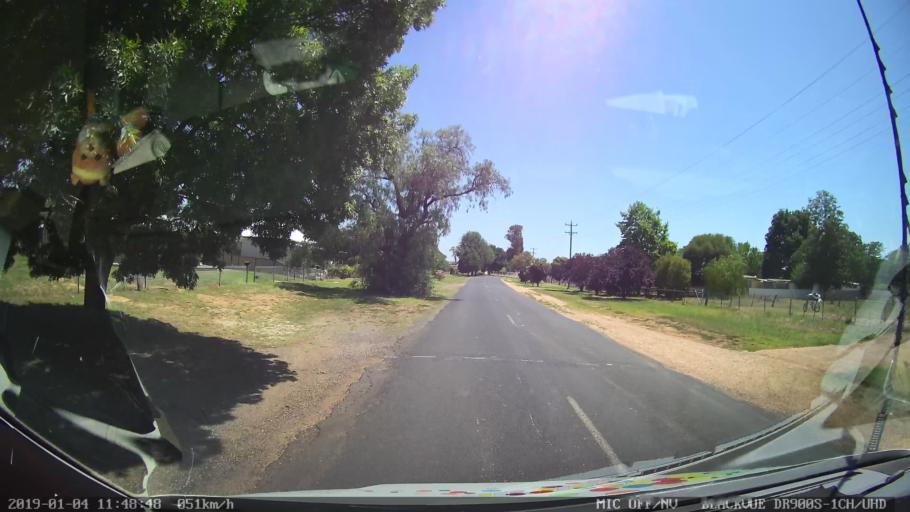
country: AU
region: New South Wales
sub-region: Cabonne
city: Molong
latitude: -32.9238
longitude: 148.7548
